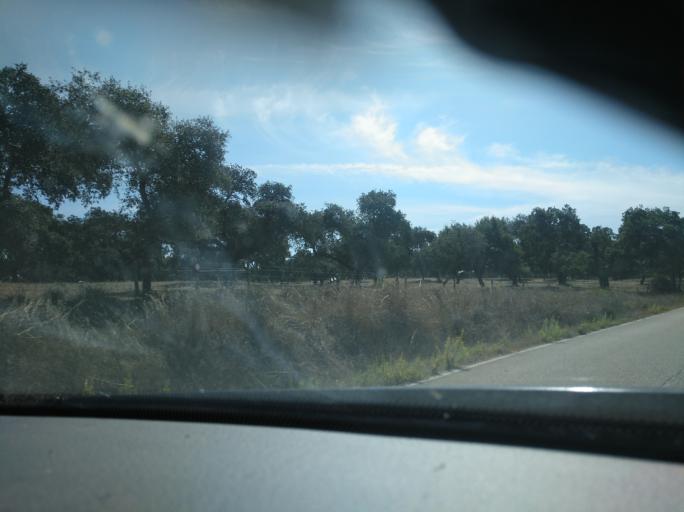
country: PT
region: Evora
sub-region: Arraiolos
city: Arraiolos
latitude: 38.6847
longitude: -8.0910
